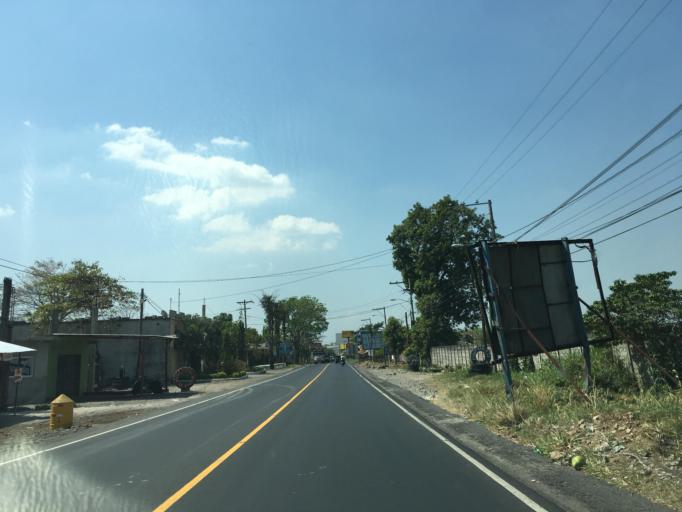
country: GT
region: Escuintla
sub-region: Municipio de Escuintla
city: Escuintla
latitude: 14.2976
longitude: -90.7947
